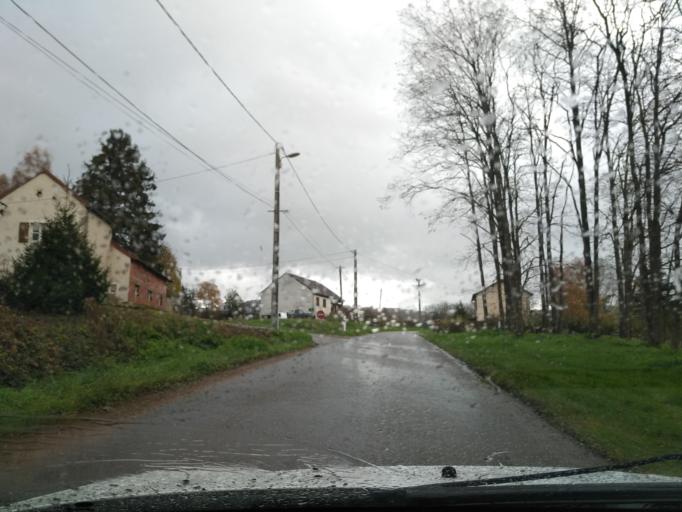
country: FR
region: Bourgogne
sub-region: Departement de Saone-et-Loire
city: Saint-Leger-sur-Dheune
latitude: 46.8230
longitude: 4.6051
